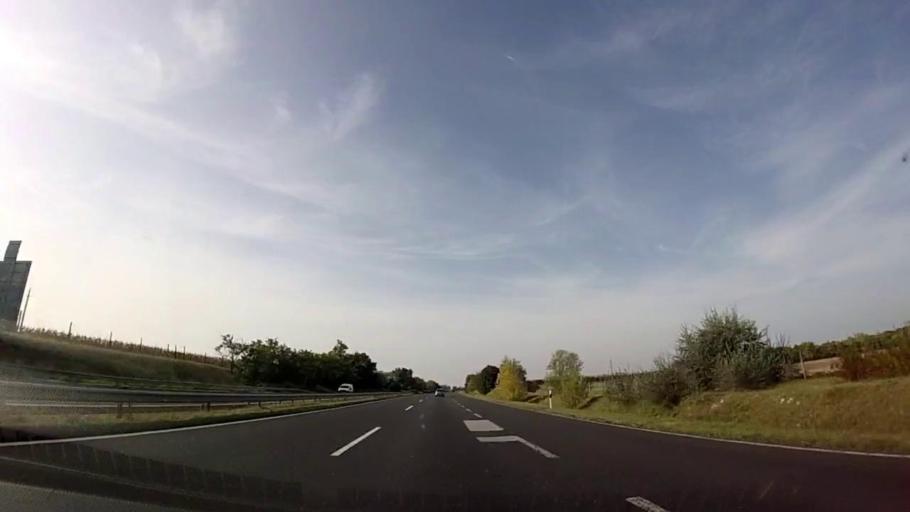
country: HU
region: Somogy
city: Balatonszabadi
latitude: 46.9275
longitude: 18.1327
